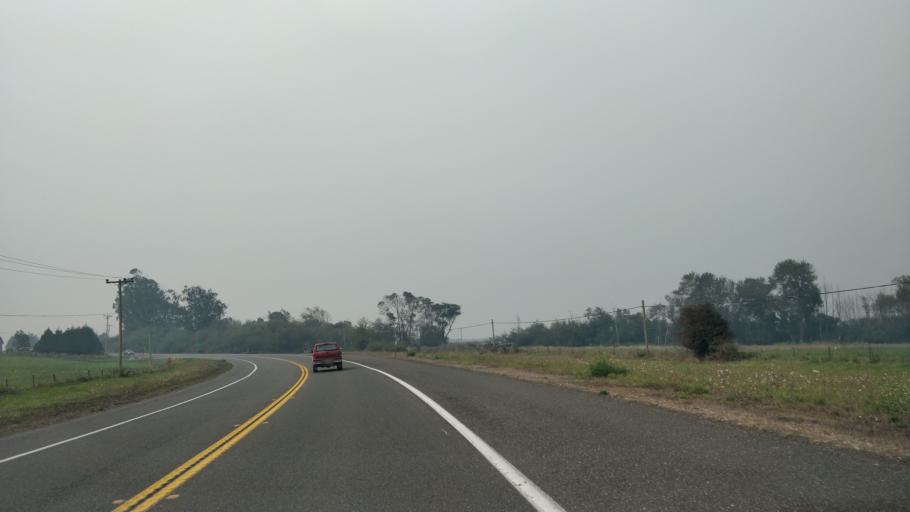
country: US
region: California
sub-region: Humboldt County
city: Ferndale
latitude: 40.5958
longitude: -124.2439
